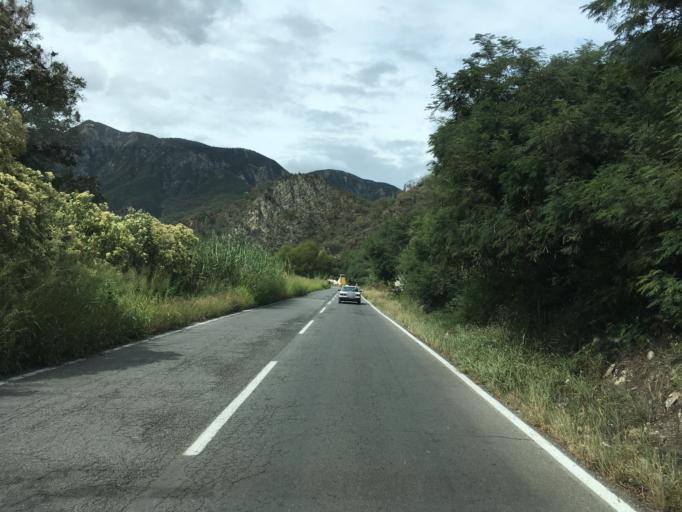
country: MX
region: Hidalgo
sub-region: San Agustin Metzquititlan
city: Mezquititlan
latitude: 20.5224
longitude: -98.7189
